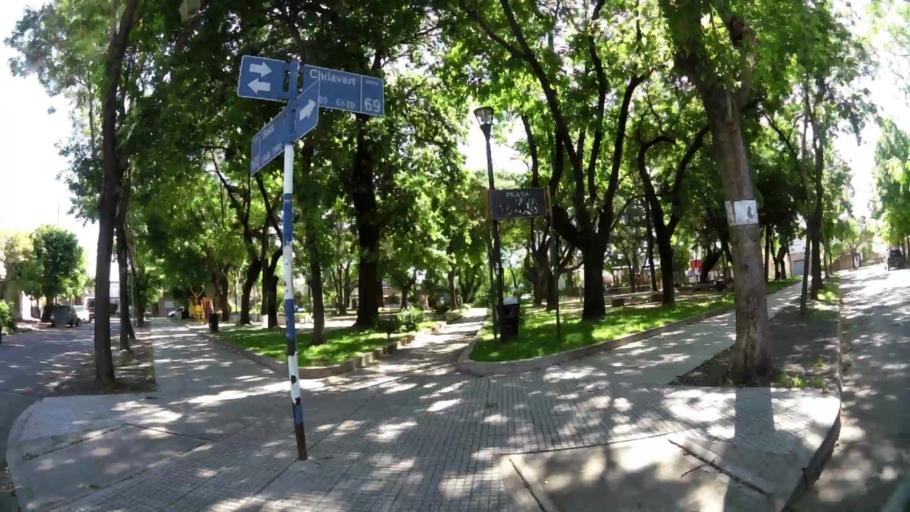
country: AR
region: Buenos Aires
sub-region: Partido de General San Martin
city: General San Martin
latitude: -34.5404
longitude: -58.5740
